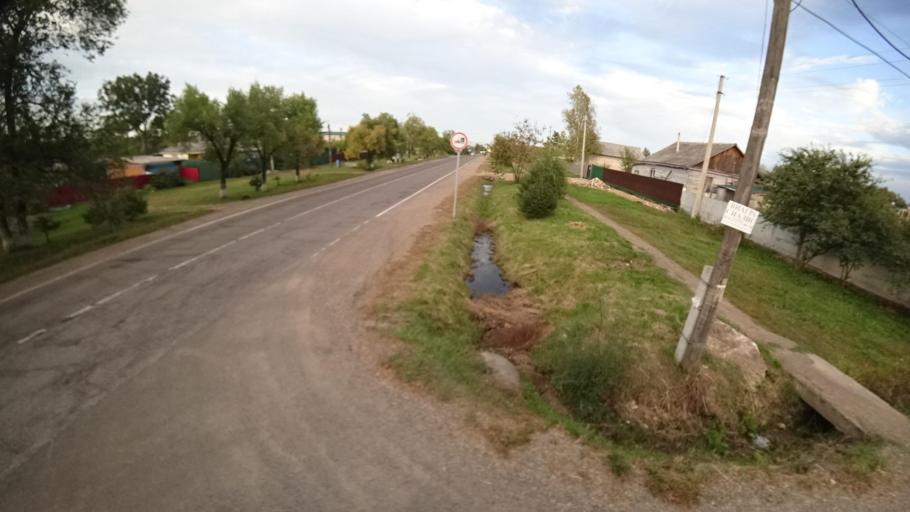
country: RU
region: Primorskiy
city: Yakovlevka
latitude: 44.4240
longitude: 133.4655
